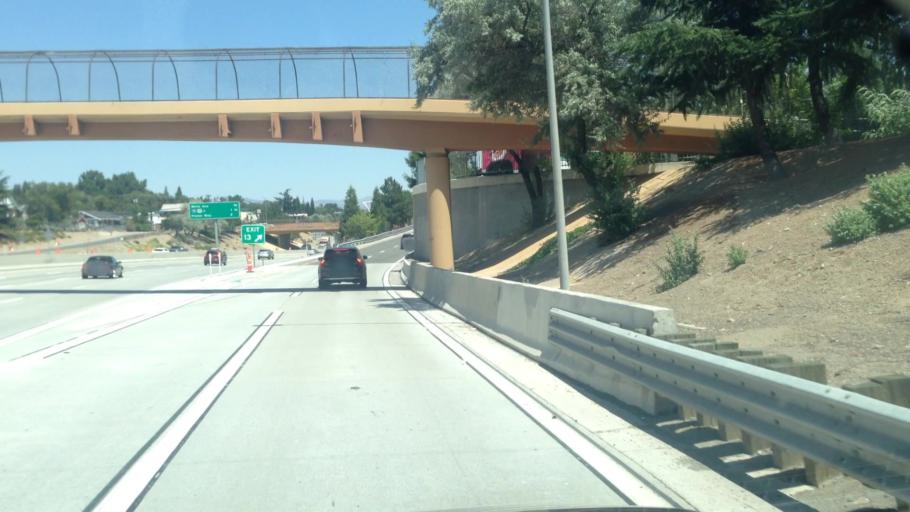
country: US
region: Nevada
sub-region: Washoe County
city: Reno
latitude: 39.5333
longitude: -119.8201
